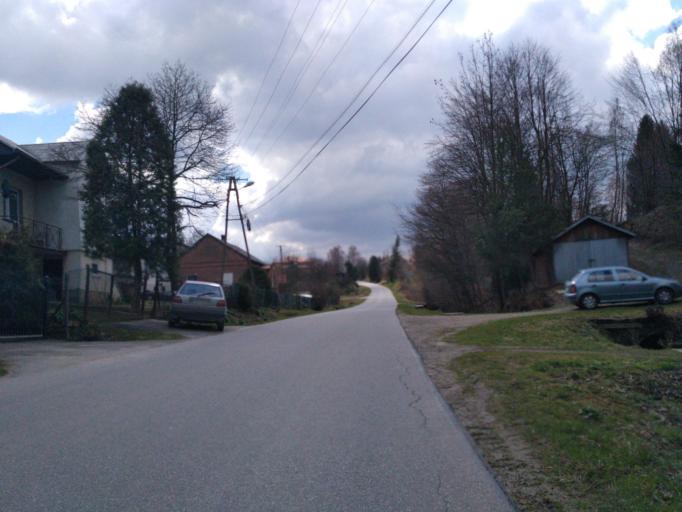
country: PL
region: Subcarpathian Voivodeship
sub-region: Powiat brzozowski
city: Dydnia
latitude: 49.6587
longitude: 22.2000
